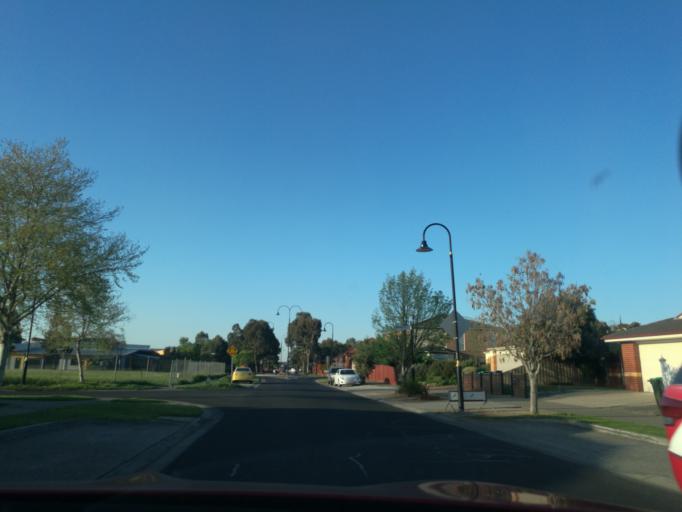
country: AU
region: Victoria
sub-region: Wyndham
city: Williams Landing
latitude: -37.8825
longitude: 144.7439
